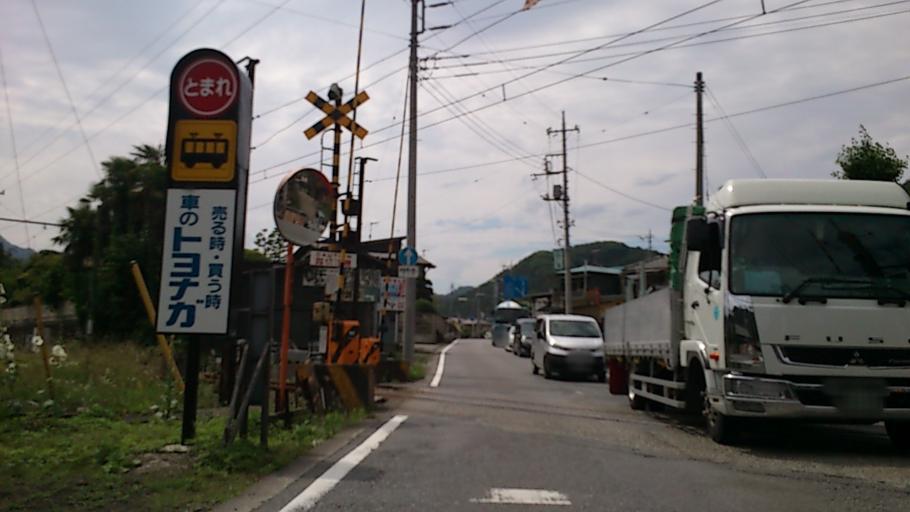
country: JP
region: Gunma
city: Tomioka
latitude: 36.2108
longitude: 138.7897
